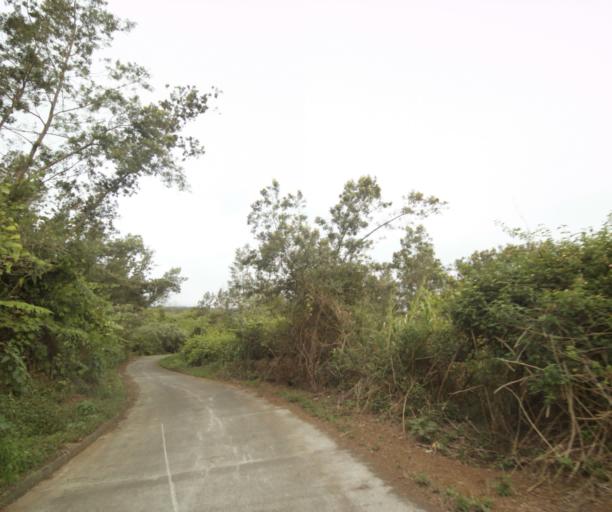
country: RE
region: Reunion
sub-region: Reunion
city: Saint-Paul
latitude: -21.0166
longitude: 55.3528
